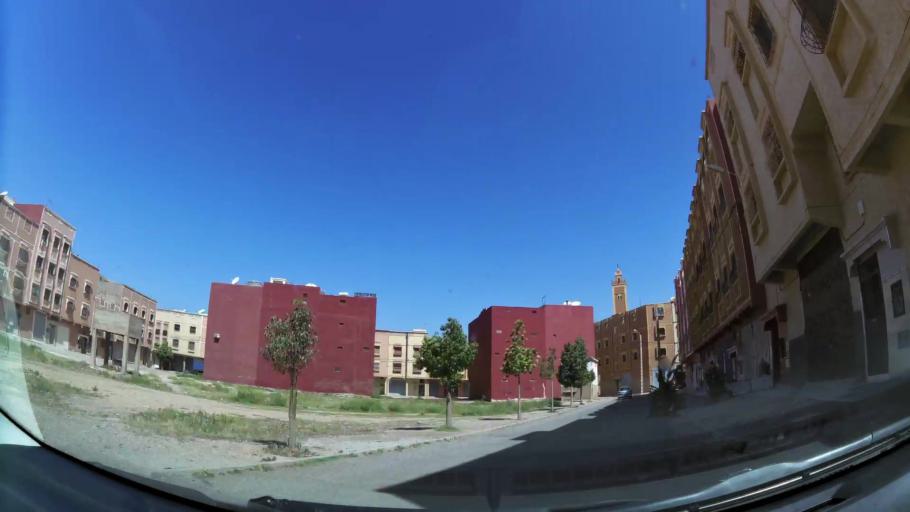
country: MA
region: Souss-Massa-Draa
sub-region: Inezgane-Ait Mellou
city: Inezgane
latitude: 30.3311
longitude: -9.5054
